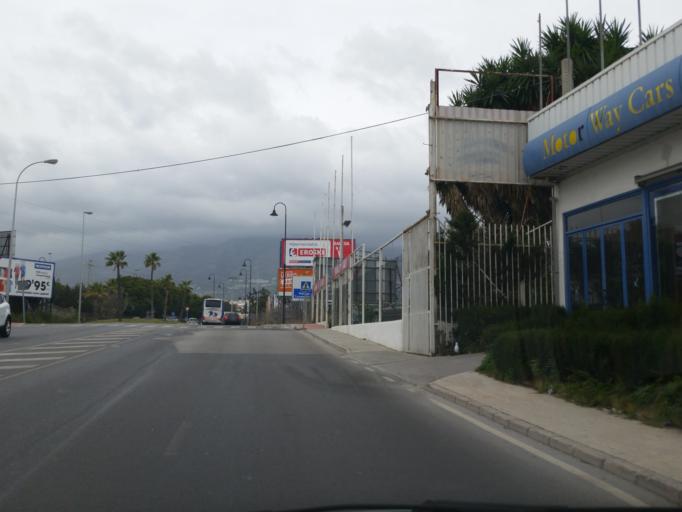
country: ES
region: Andalusia
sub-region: Provincia de Malaga
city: Fuengirola
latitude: 36.5486
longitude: -4.6268
